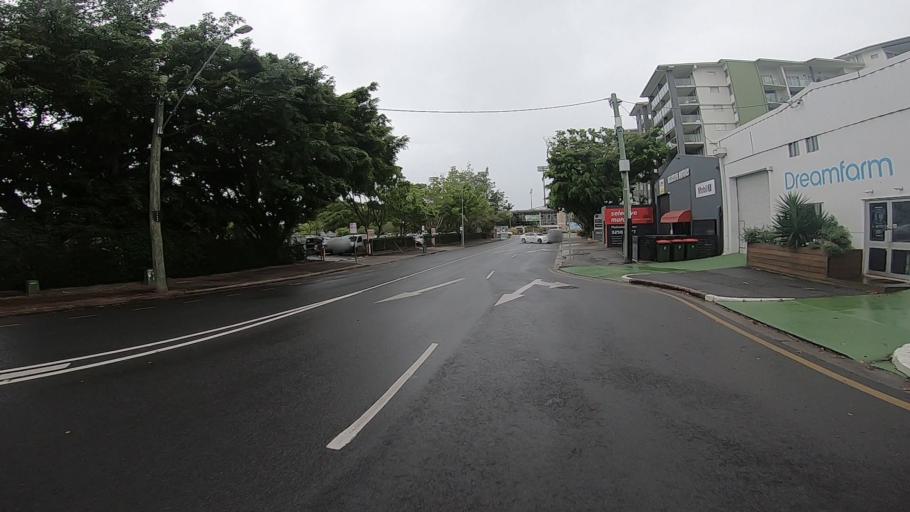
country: AU
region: Queensland
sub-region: Brisbane
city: Ascot
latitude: -27.4407
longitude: 153.0463
